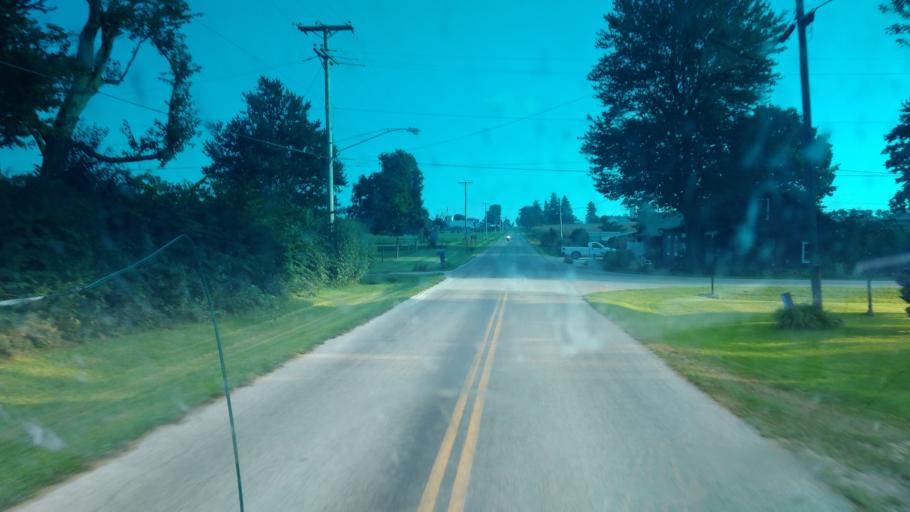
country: US
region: Ohio
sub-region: Crawford County
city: Bucyrus
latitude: 40.8703
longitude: -82.8731
